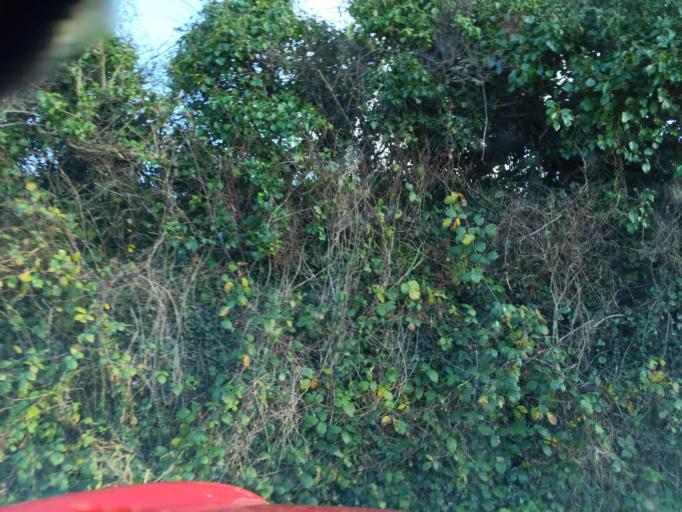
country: GB
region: England
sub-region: Cornwall
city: Fowey
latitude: 50.3265
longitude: -4.6258
